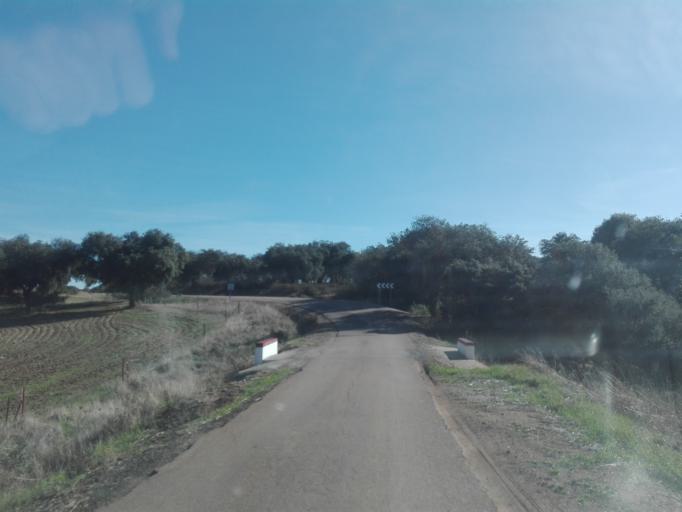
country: ES
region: Extremadura
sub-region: Provincia de Badajoz
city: Valencia de las Torres
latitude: 38.3371
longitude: -5.9306
